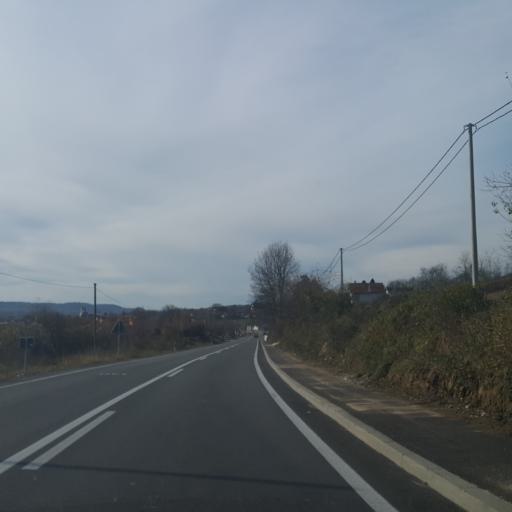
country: RS
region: Central Serbia
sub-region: Sumadijski Okrug
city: Arangelovac
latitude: 44.3348
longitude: 20.4838
